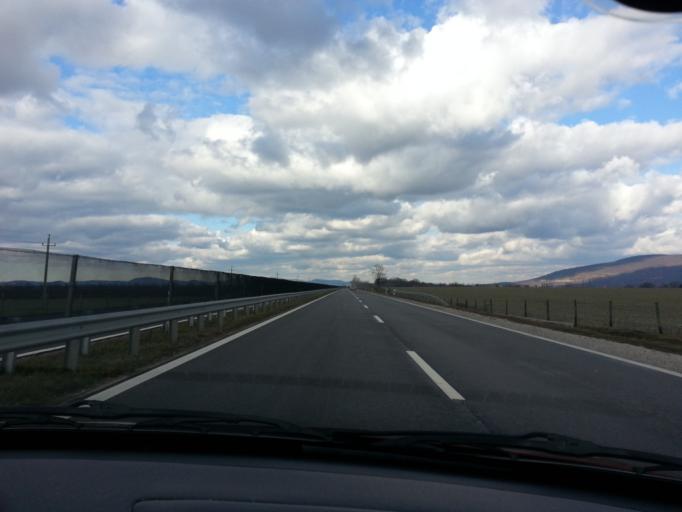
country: HU
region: Heves
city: Zagyvaszanto
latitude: 47.7784
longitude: 19.6609
